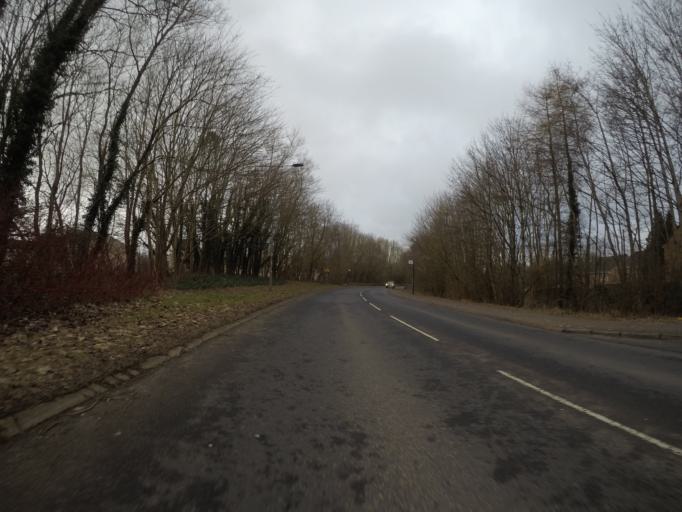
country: GB
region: Scotland
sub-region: North Ayrshire
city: Irvine
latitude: 55.6313
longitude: -4.6398
